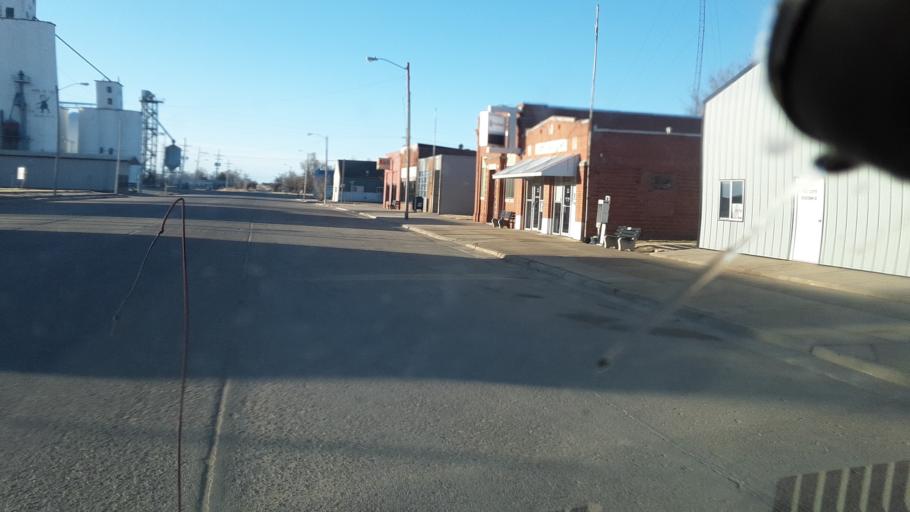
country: US
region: Kansas
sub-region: Rice County
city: Lyons
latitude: 38.3542
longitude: -98.3495
